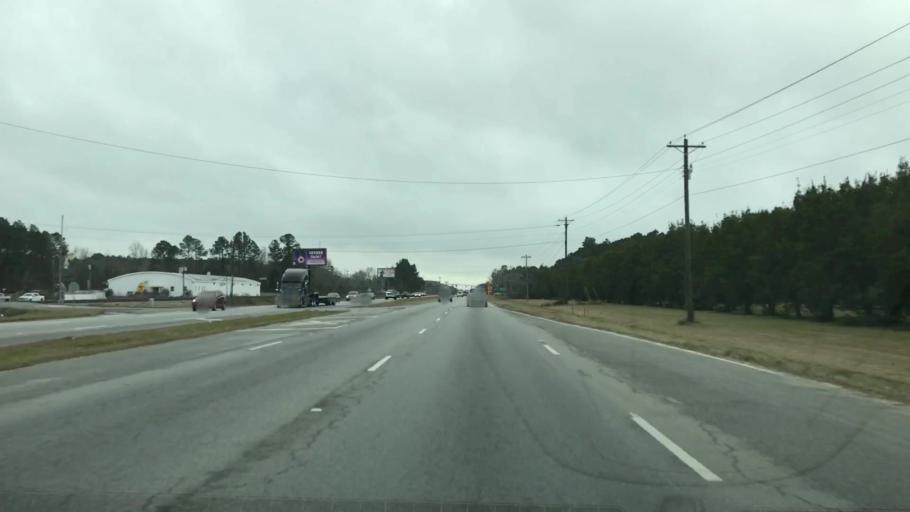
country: US
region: South Carolina
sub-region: Berkeley County
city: Goose Creek
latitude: 33.0379
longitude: -80.0339
